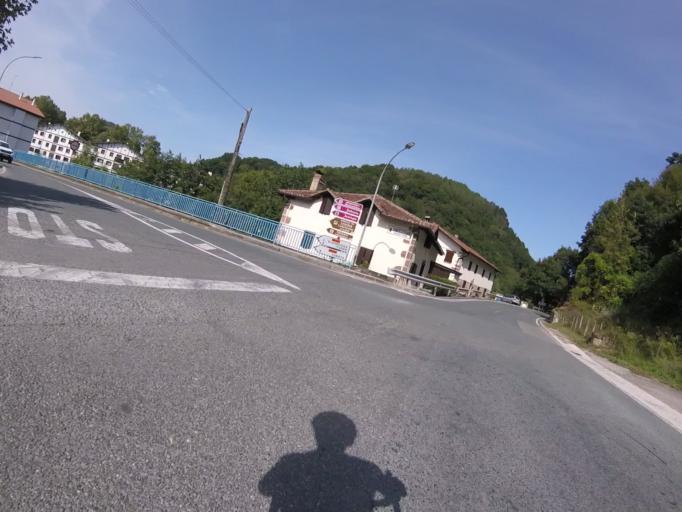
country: ES
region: Navarre
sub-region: Provincia de Navarra
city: Doneztebe
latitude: 43.1346
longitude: -1.6643
